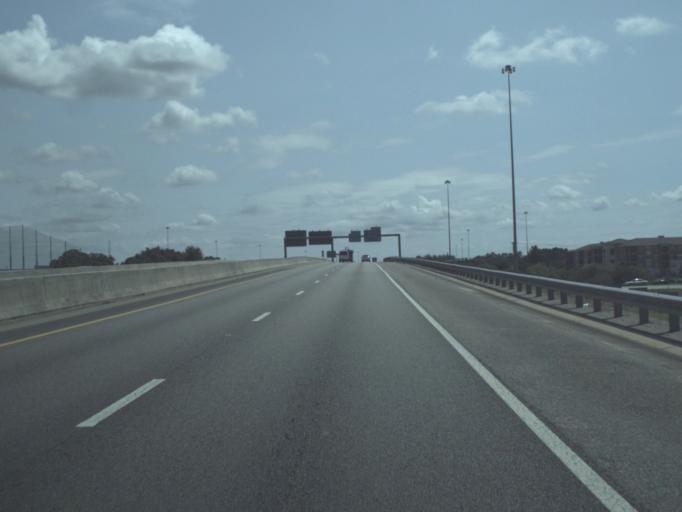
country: US
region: Florida
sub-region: Hillsborough County
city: Progress Village
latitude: 27.9288
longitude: -82.3401
